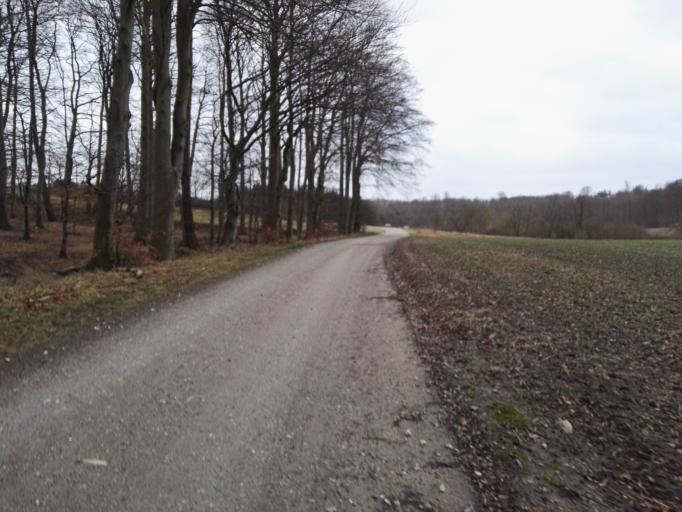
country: DK
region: Zealand
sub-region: Lejre Kommune
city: Lejre
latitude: 55.6408
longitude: 11.9301
